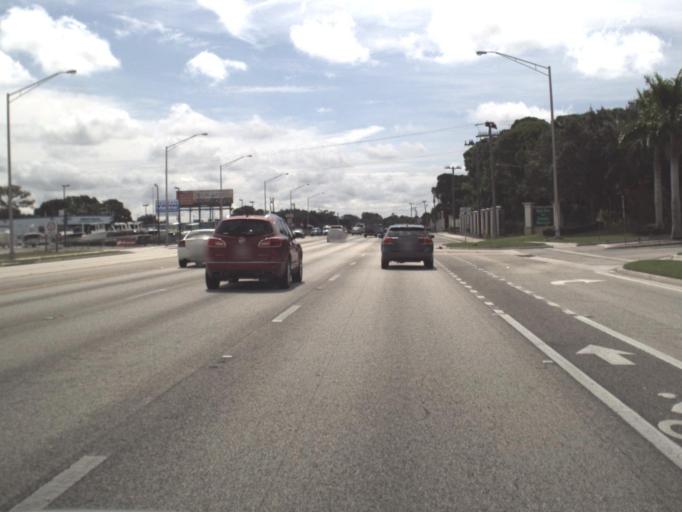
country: US
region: Florida
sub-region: Manatee County
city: Whitfield
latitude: 27.3936
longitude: -82.5619
